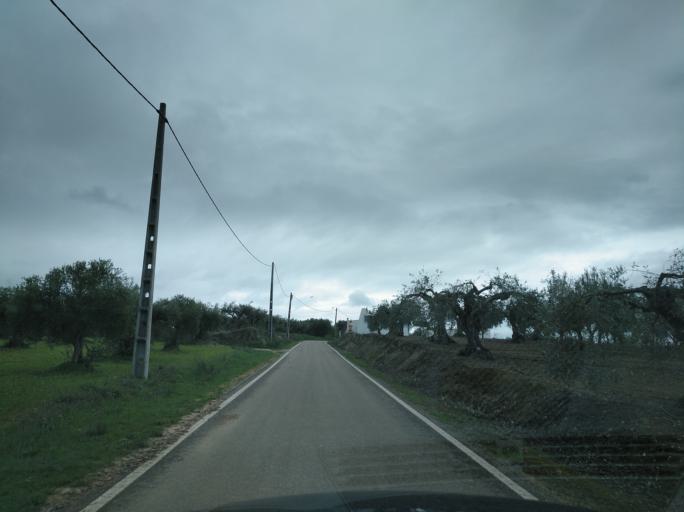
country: PT
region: Portalegre
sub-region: Campo Maior
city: Campo Maior
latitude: 38.9934
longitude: -7.0490
